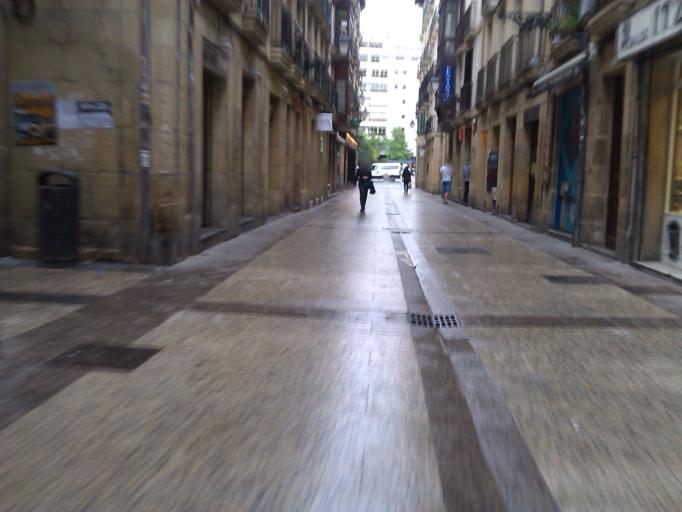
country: ES
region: Basque Country
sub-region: Provincia de Guipuzcoa
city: San Sebastian
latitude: 43.3230
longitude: -1.9854
